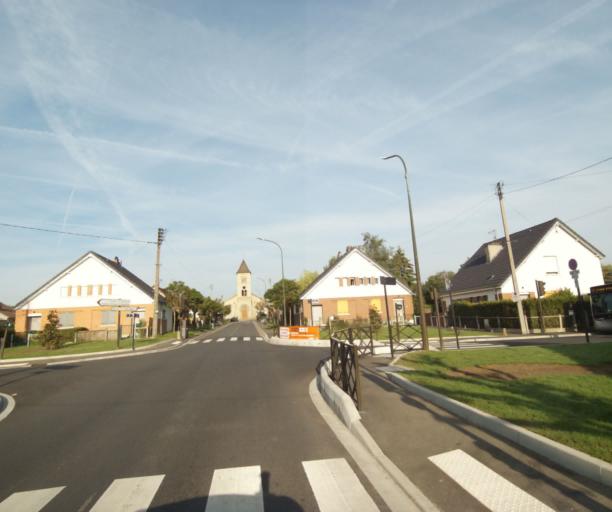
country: FR
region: Ile-de-France
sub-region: Departement du Val-d'Oise
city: Saint-Gratien
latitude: 48.9551
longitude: 2.2884
